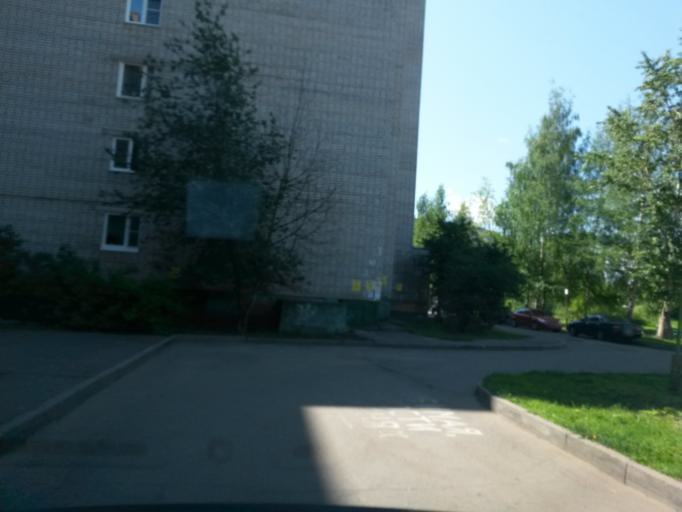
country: RU
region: Jaroslavl
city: Yaroslavl
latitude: 57.7008
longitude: 39.7686
